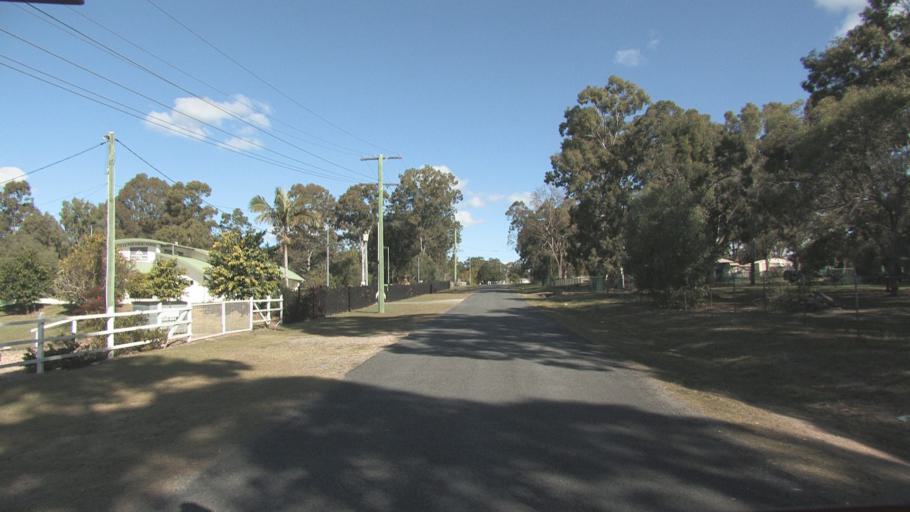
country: AU
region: Queensland
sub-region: Logan
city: Logan Reserve
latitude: -27.7139
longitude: 153.1113
